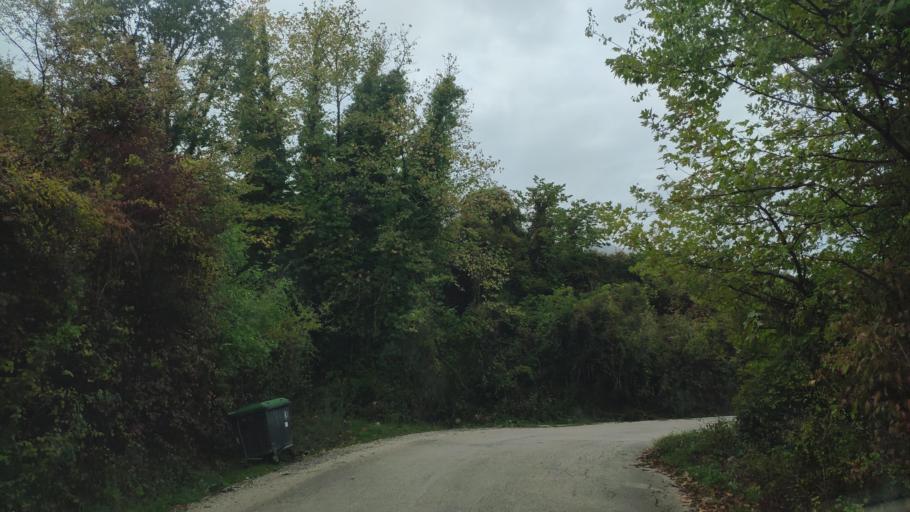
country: GR
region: Epirus
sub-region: Nomos Thesprotias
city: Paramythia
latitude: 39.4601
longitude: 20.6762
